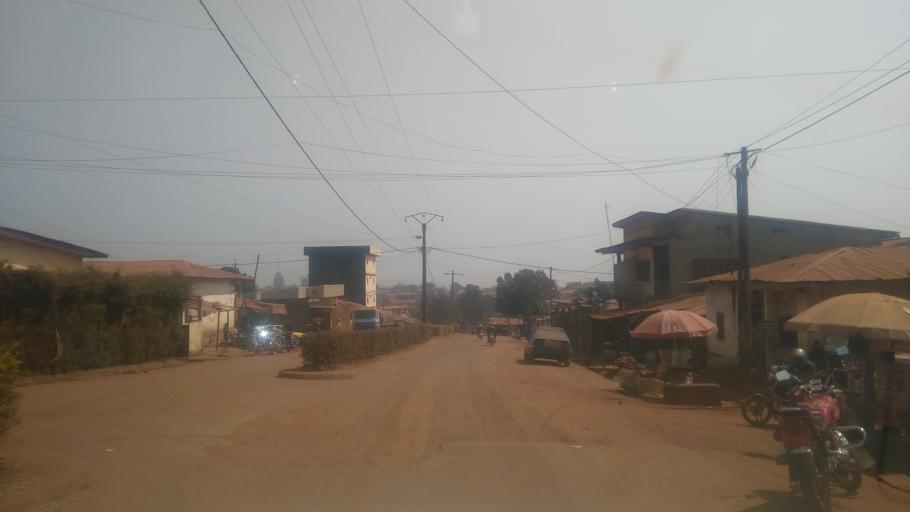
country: CM
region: West
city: Bafoussam
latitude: 5.4851
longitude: 10.4146
